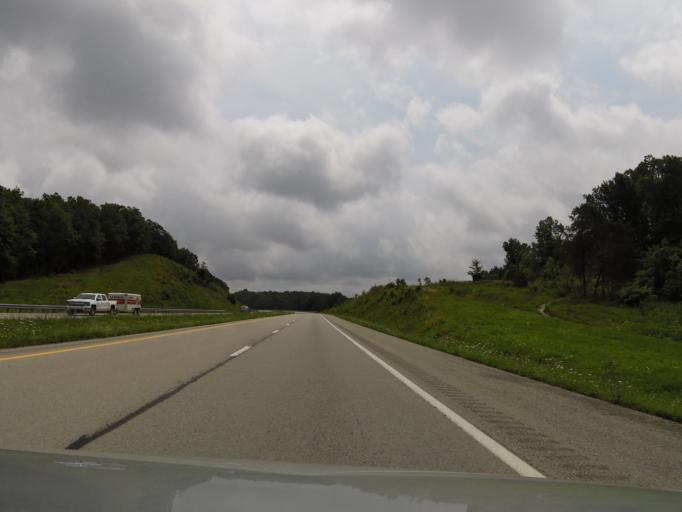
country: US
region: Kentucky
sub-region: Ohio County
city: Oak Grove
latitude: 37.3851
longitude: -86.6612
